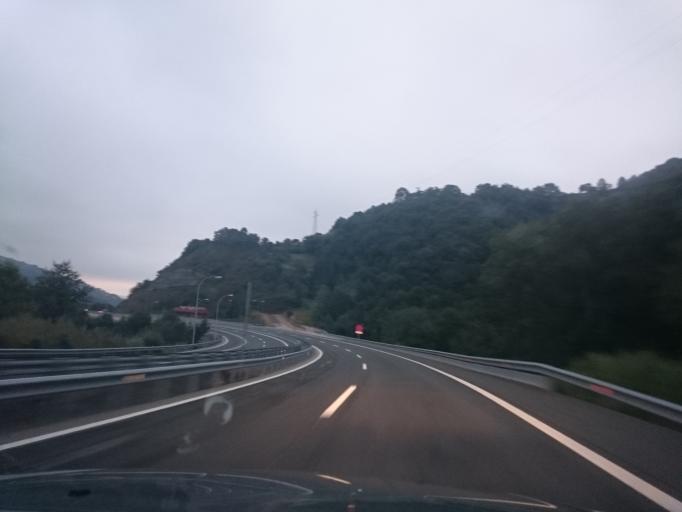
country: ES
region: Asturias
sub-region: Province of Asturias
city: Pola de Lena
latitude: 43.0870
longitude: -5.8232
